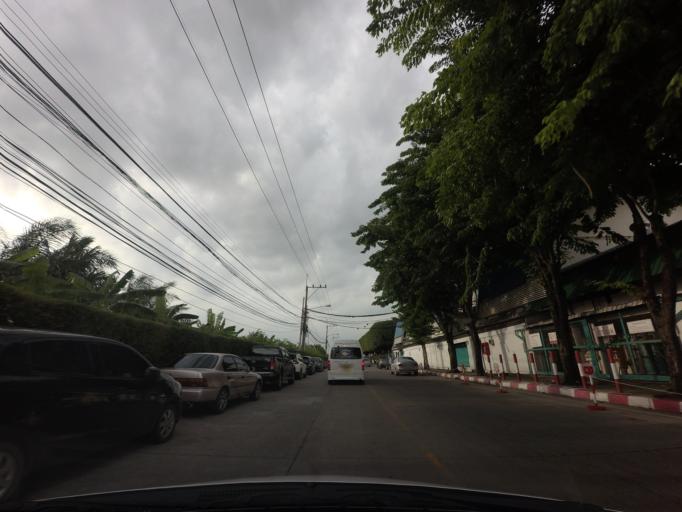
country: TH
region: Pathum Thani
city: Thanyaburi
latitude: 13.9921
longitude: 100.6746
